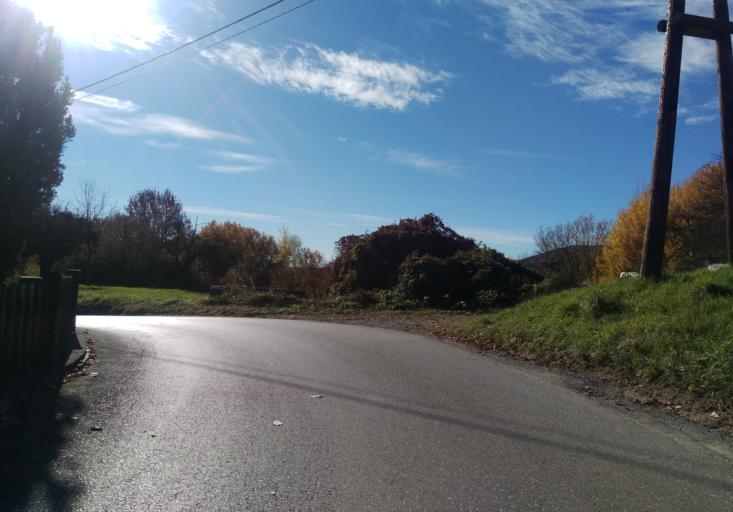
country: AT
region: Styria
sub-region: Graz Stadt
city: Mariatrost
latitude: 47.1222
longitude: 15.4912
